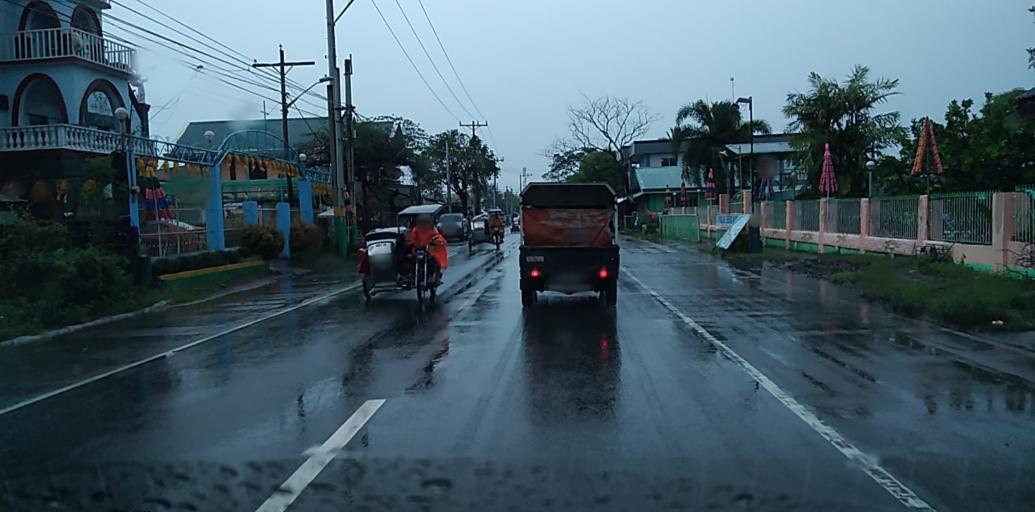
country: PH
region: Central Luzon
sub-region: Province of Bulacan
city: Bulualto
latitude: 15.2108
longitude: 120.9557
